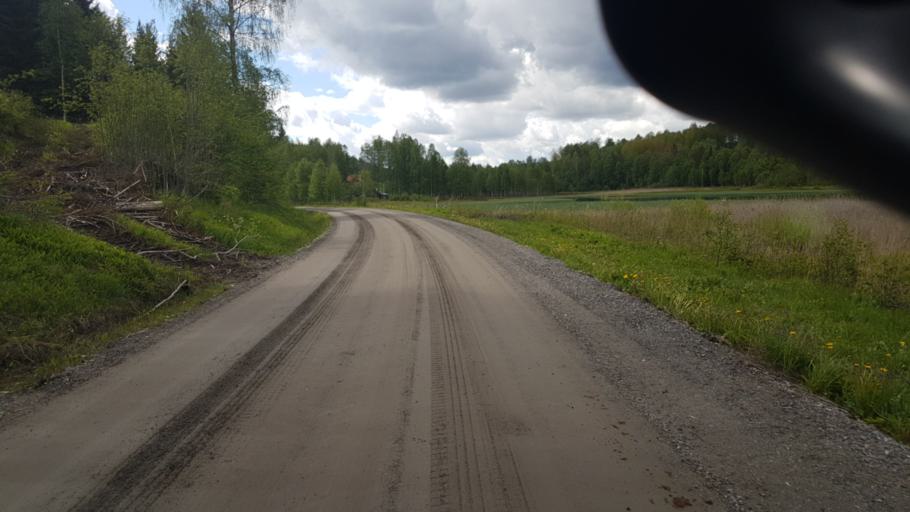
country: NO
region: Ostfold
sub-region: Romskog
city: Romskog
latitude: 59.6753
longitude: 11.9329
